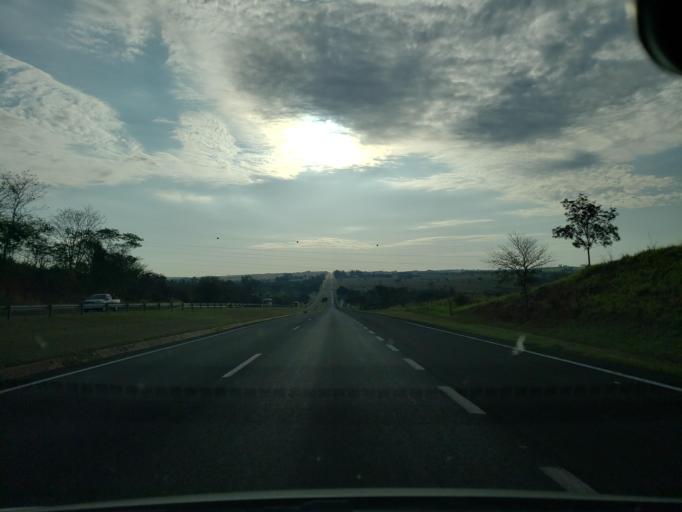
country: BR
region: Sao Paulo
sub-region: Mirandopolis
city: Mirandopolis
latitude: -21.0849
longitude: -51.0648
